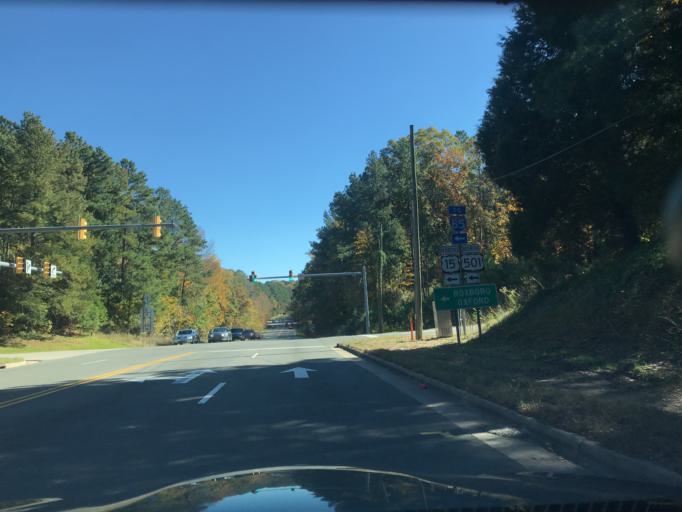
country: US
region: North Carolina
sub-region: Durham County
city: Durham
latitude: 35.9987
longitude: -78.9582
